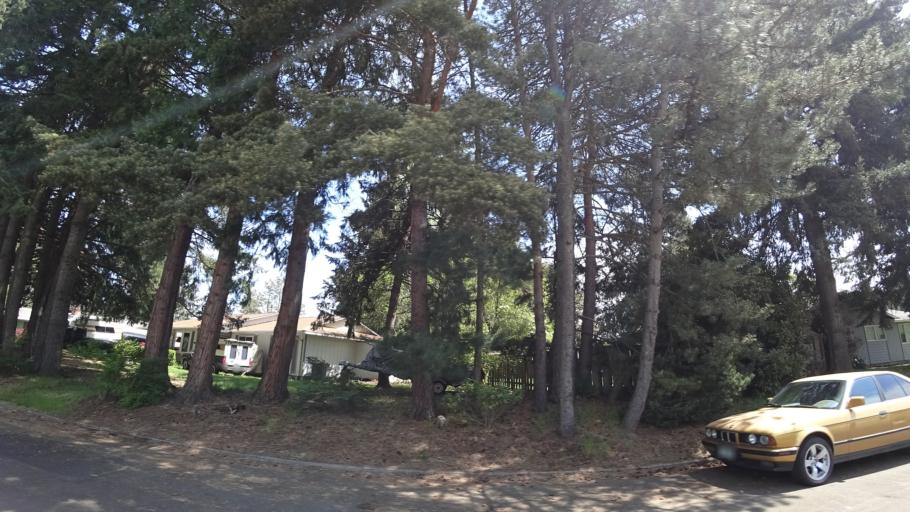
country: US
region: Oregon
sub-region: Washington County
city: Aloha
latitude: 45.4787
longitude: -122.8854
